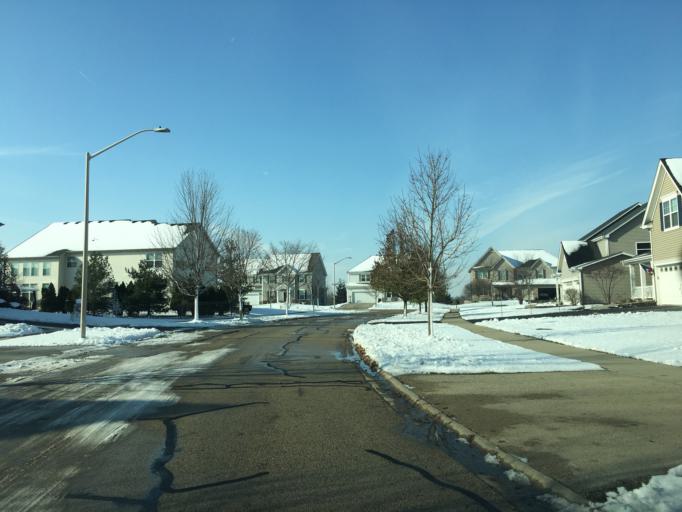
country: US
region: Illinois
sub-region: Will County
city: Plainfield
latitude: 41.6553
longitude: -88.1768
